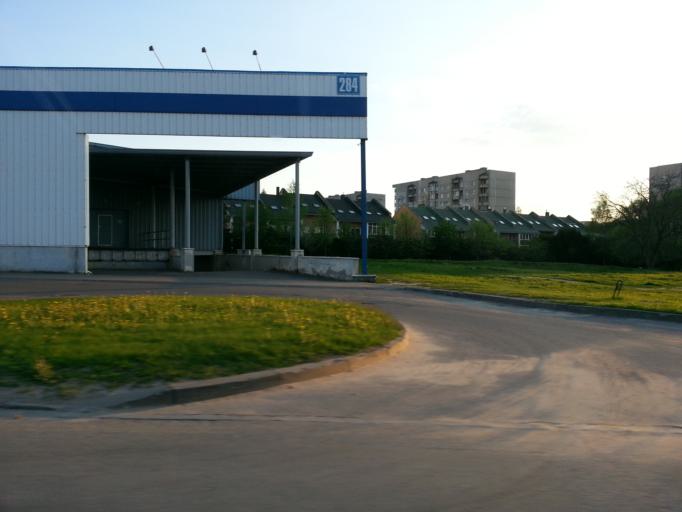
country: LT
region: Vilnius County
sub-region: Vilnius
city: Fabijoniskes
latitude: 54.7334
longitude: 25.2351
